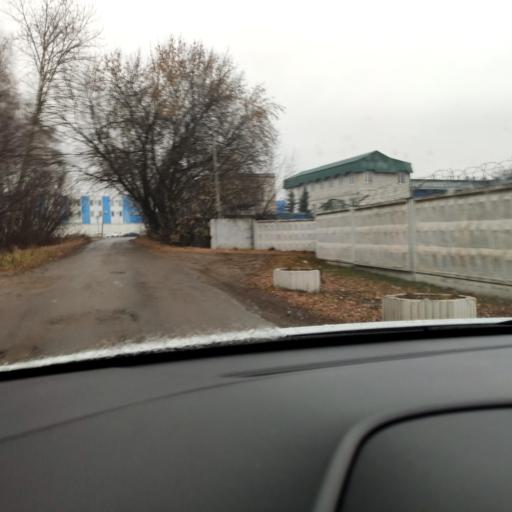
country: RU
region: Tatarstan
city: Staroye Arakchino
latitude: 55.8539
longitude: 49.0256
